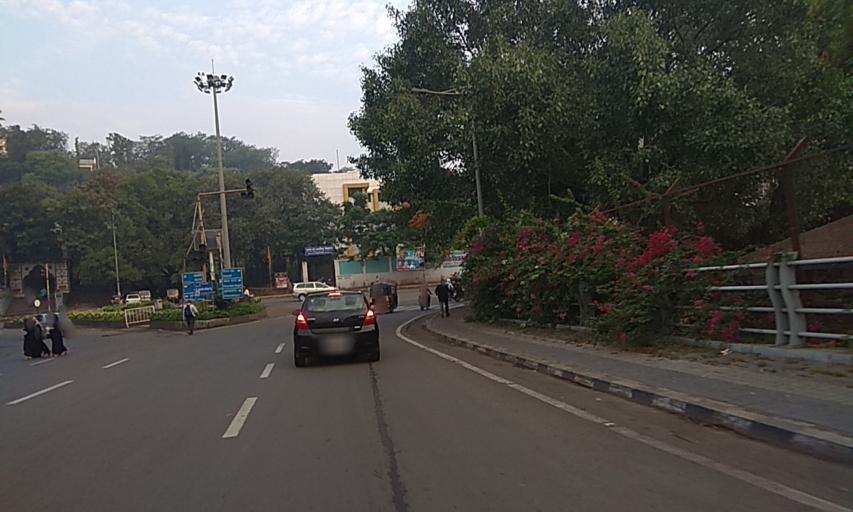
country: IN
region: Maharashtra
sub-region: Pune Division
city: Shivaji Nagar
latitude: 18.5446
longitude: 73.8834
